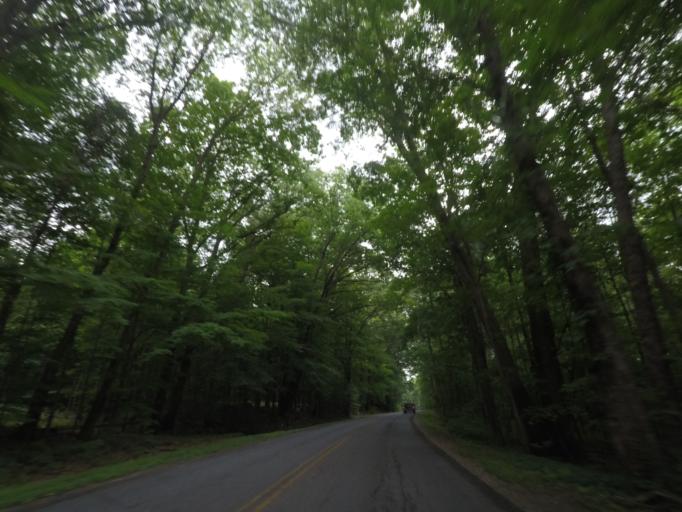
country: US
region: New York
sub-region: Saratoga County
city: Stillwater
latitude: 42.8443
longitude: -73.5380
